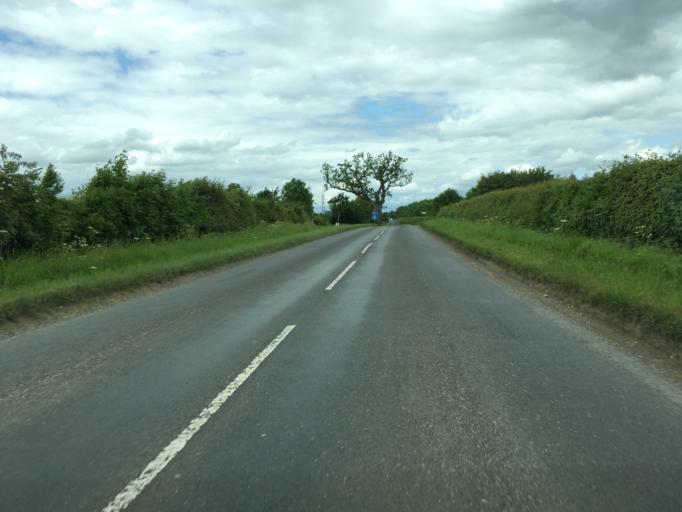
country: GB
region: England
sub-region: Gloucestershire
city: Cirencester
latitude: 51.6939
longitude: -1.9665
